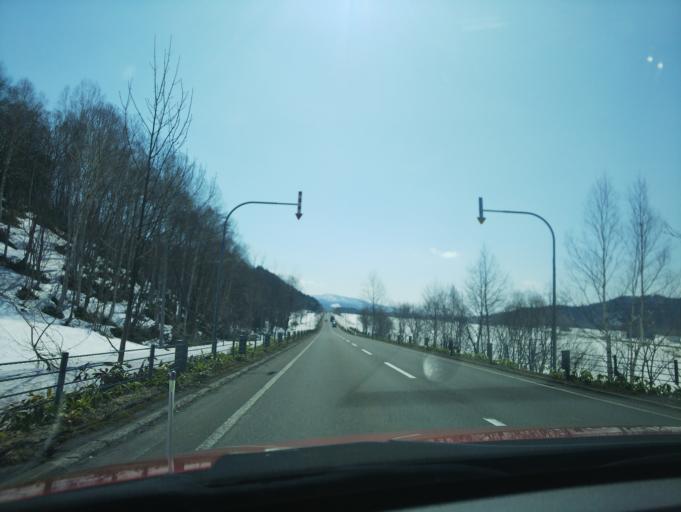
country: JP
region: Hokkaido
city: Nayoro
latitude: 44.6351
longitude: 142.2775
